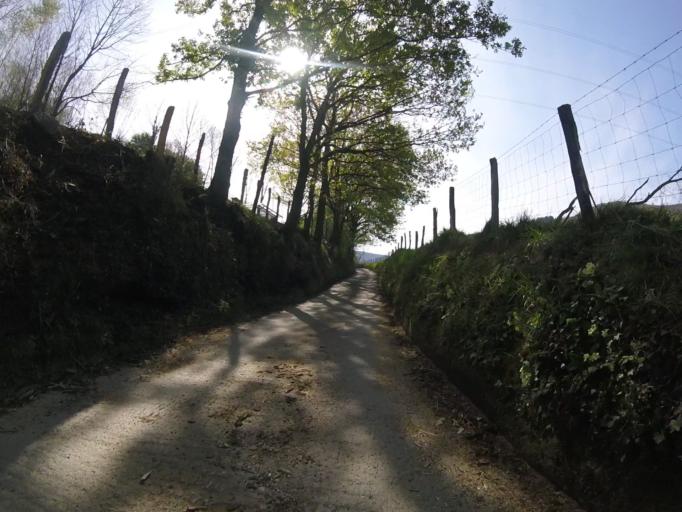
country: ES
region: Basque Country
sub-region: Provincia de Guipuzcoa
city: Errenteria
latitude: 43.2793
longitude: -1.8463
